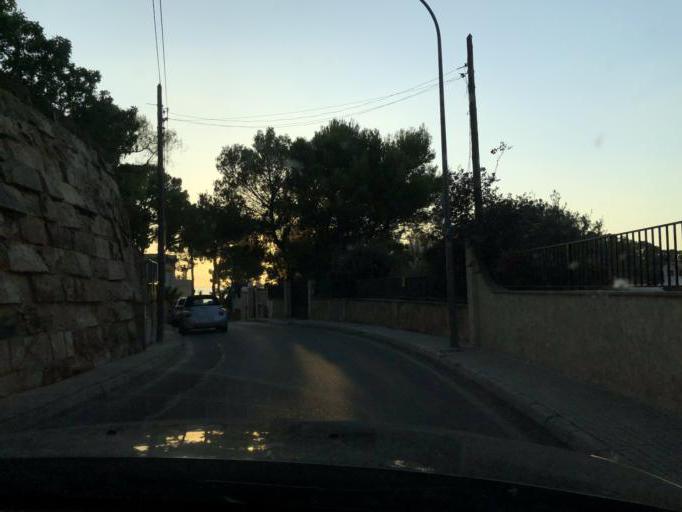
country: ES
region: Balearic Islands
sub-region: Illes Balears
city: Santa Ponsa
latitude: 39.5280
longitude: 2.4696
